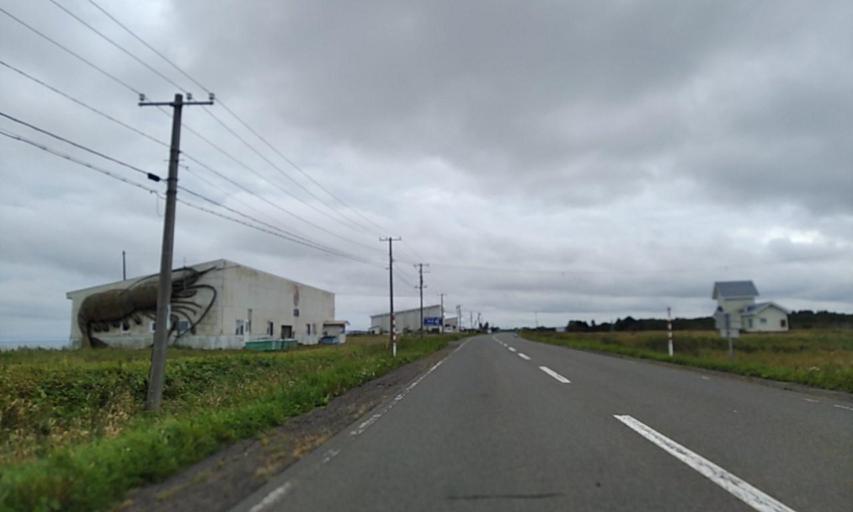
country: JP
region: Hokkaido
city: Shibetsu
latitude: 43.4064
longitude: 145.2752
